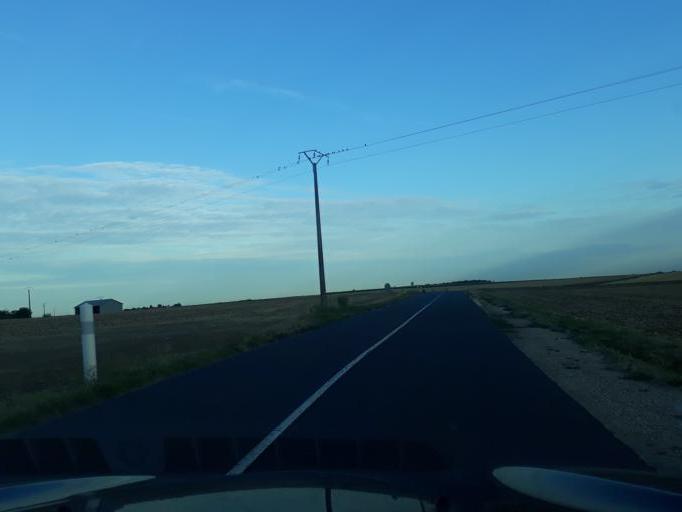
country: FR
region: Centre
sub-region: Departement du Loiret
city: Epieds-en-Beauce
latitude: 47.8926
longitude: 1.6242
